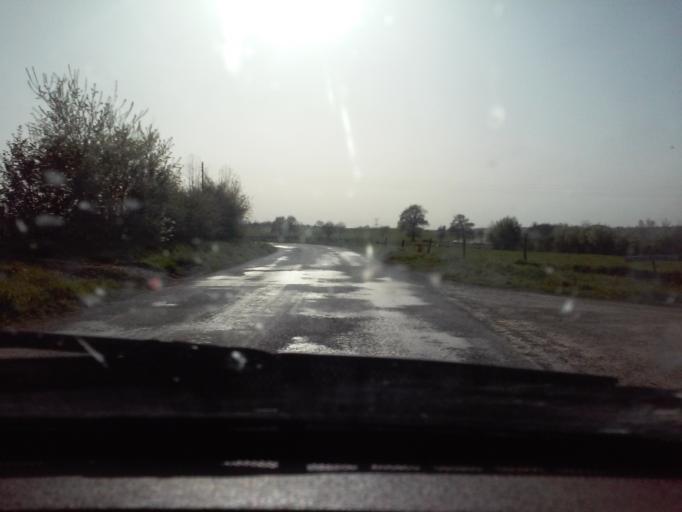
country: FR
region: Brittany
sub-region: Departement d'Ille-et-Vilaine
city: Romagne
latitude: 48.3026
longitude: -1.2694
